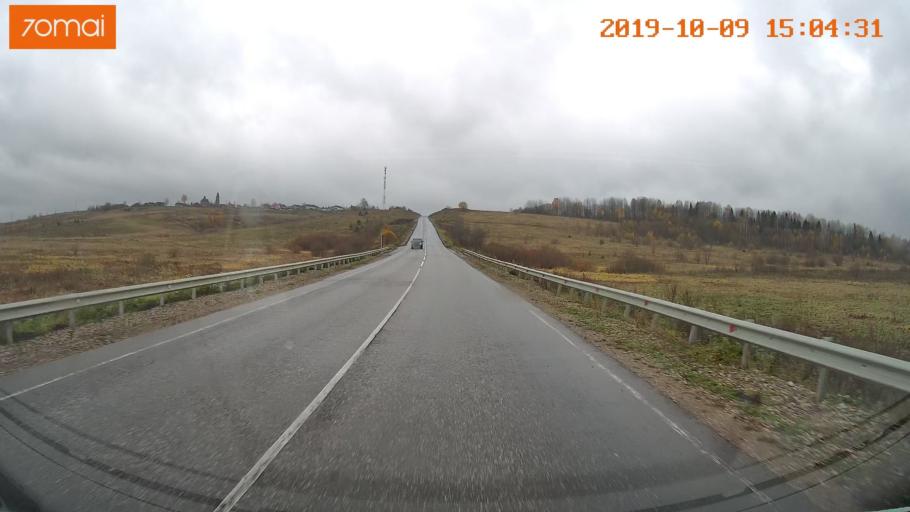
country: RU
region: Kostroma
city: Chistyye Bory
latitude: 58.2575
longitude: 41.6664
